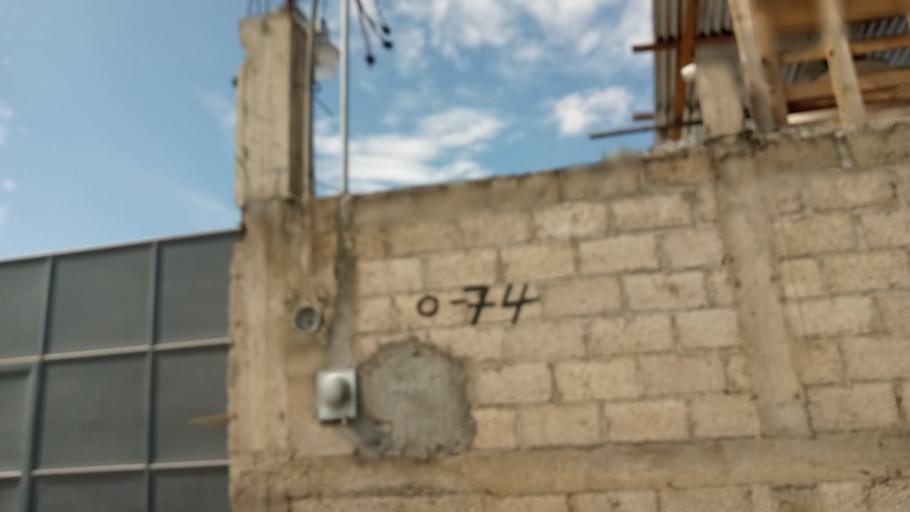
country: GT
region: Quetzaltenango
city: Quetzaltenango
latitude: 14.8468
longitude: -91.5096
